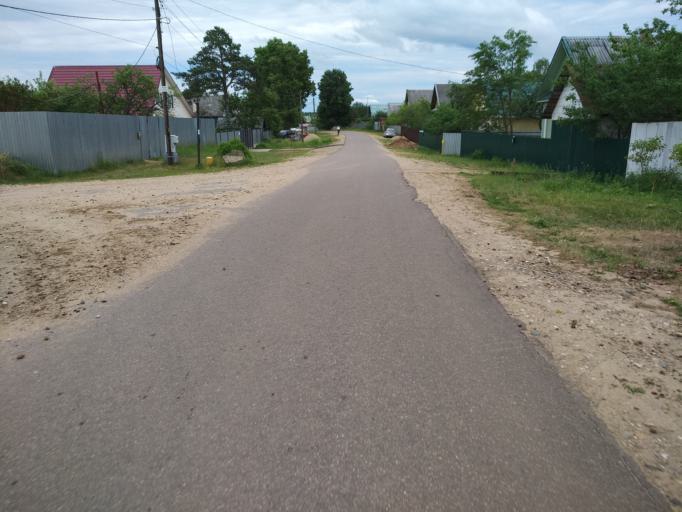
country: RU
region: Tverskaya
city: Krasnomayskiy
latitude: 57.6248
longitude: 34.4321
